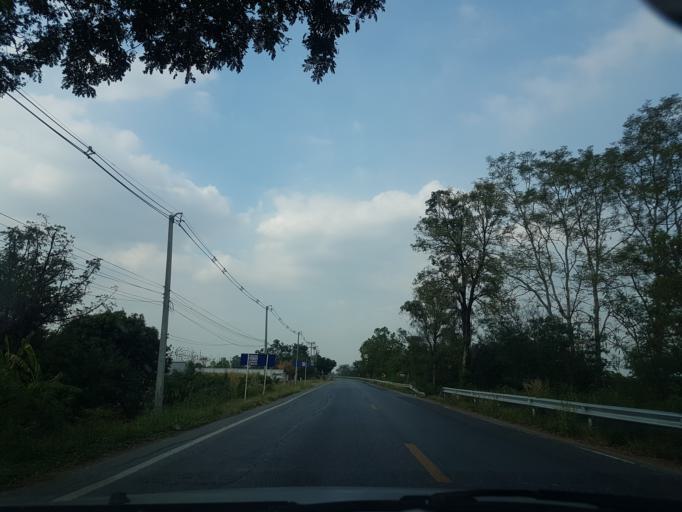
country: TH
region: Phra Nakhon Si Ayutthaya
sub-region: Amphoe Tha Ruea
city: Tha Ruea
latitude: 14.5335
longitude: 100.7453
